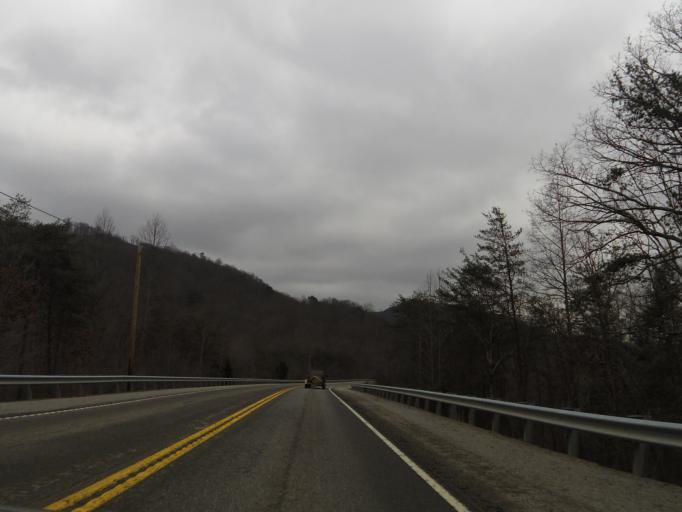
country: US
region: Tennessee
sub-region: Campbell County
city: Caryville
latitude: 36.3962
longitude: -84.2688
